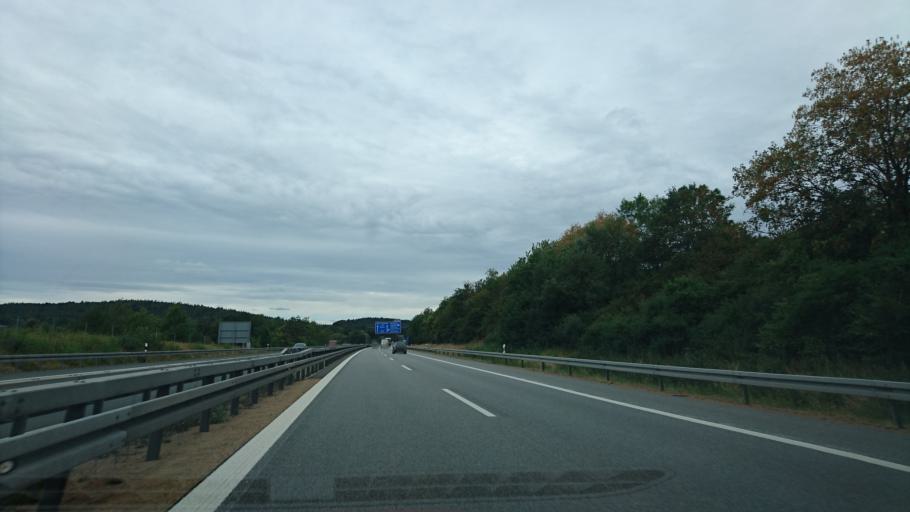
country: DE
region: Bavaria
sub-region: Upper Palatinate
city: Pfreimd
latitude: 49.5094
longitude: 12.1751
